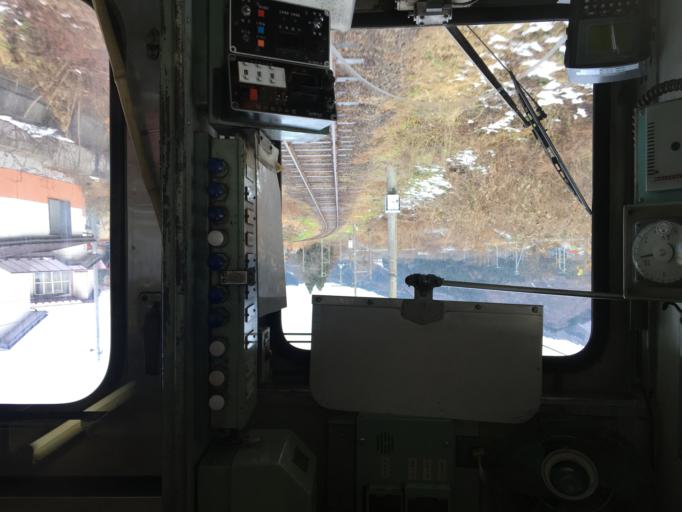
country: JP
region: Aomori
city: Hirosaki
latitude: 40.5232
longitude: 140.5597
